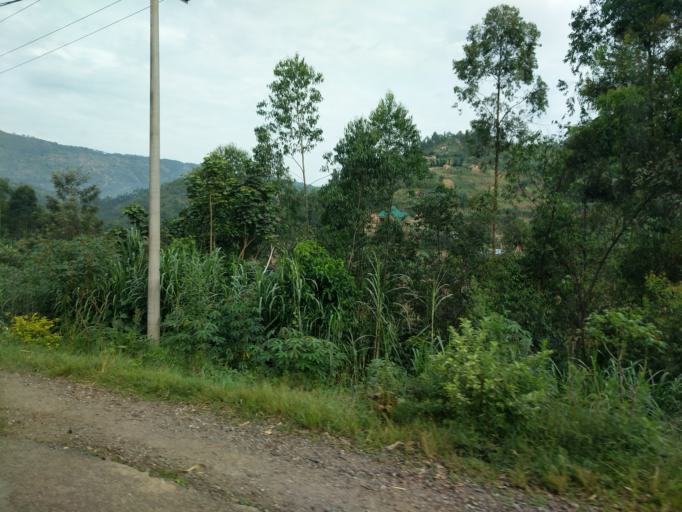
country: RW
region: Northern Province
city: Musanze
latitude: -1.6492
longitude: 29.7973
